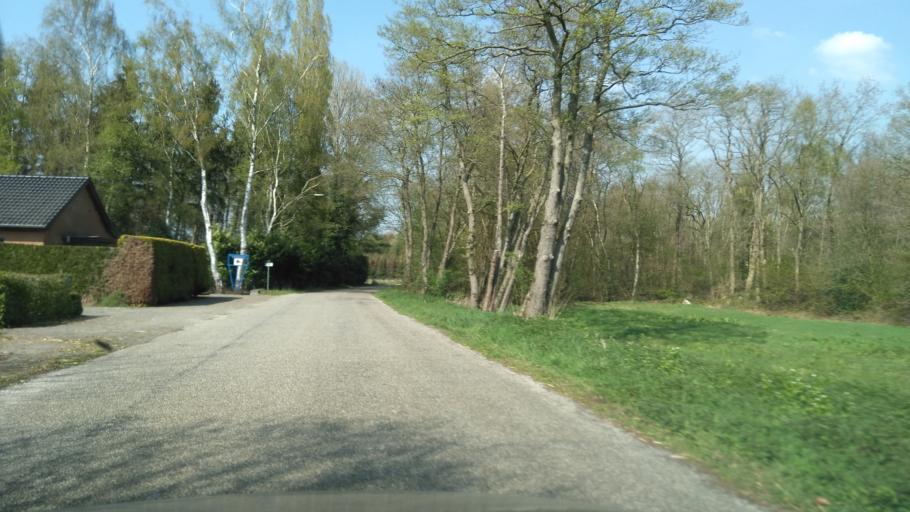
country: BE
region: Flanders
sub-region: Provincie Antwerpen
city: Baarle-Hertog
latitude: 51.4076
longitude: 4.9319
